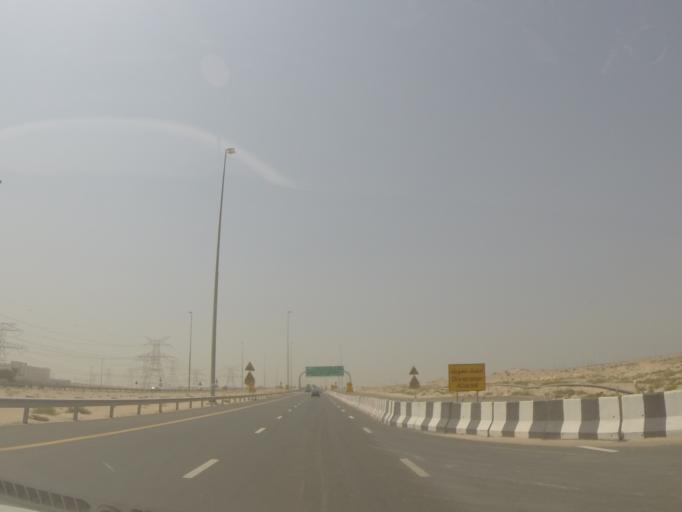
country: AE
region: Dubai
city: Dubai
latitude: 25.0102
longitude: 55.1677
